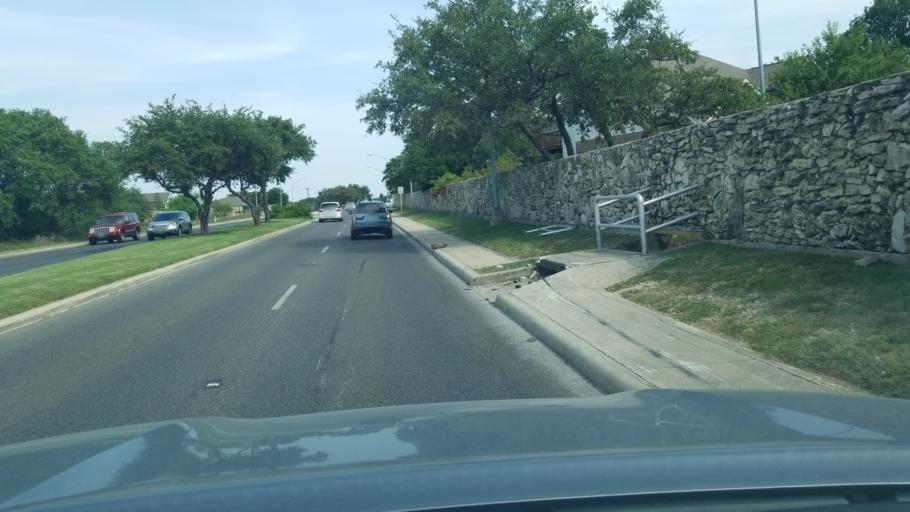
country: US
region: Texas
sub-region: Bexar County
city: Hollywood Park
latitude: 29.6465
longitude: -98.4942
